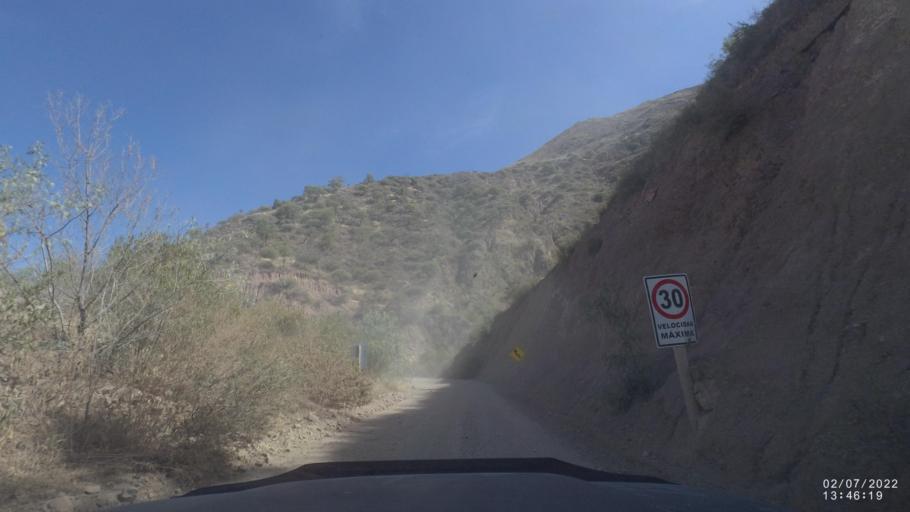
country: BO
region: Cochabamba
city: Irpa Irpa
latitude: -17.8130
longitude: -66.3666
